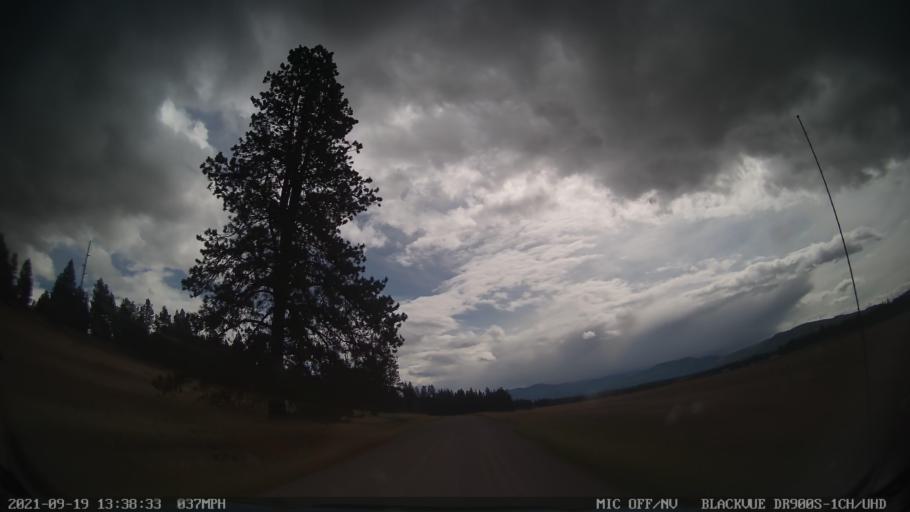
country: US
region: Montana
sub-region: Missoula County
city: Seeley Lake
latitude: 47.1040
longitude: -113.2705
